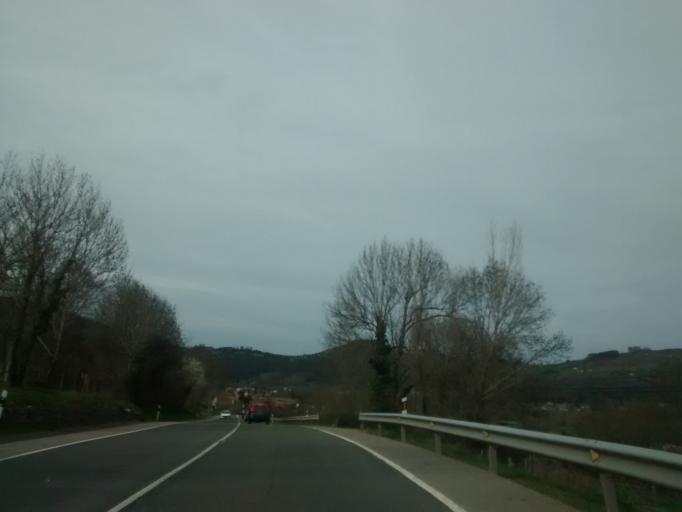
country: ES
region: Cantabria
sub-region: Provincia de Cantabria
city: Corvera
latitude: 43.2604
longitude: -3.9475
